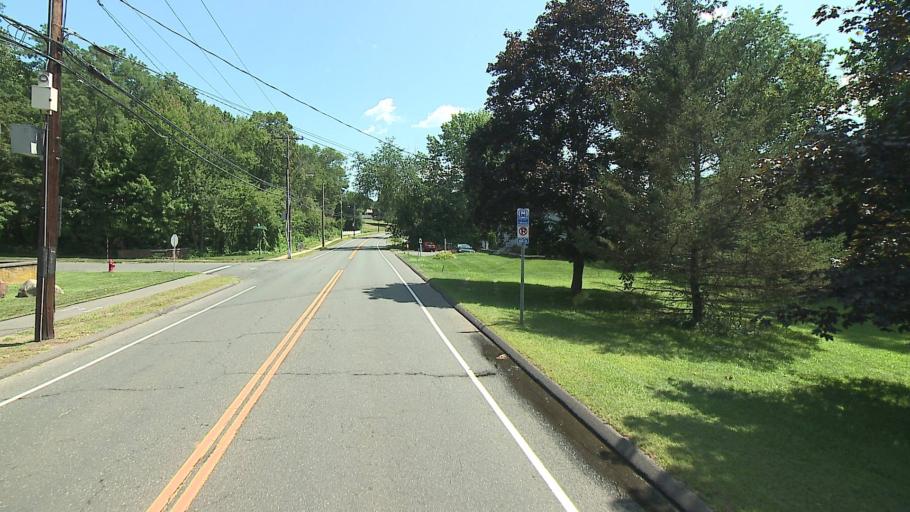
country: US
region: Connecticut
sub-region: Hartford County
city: Farmington
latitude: 41.7516
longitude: -72.8719
